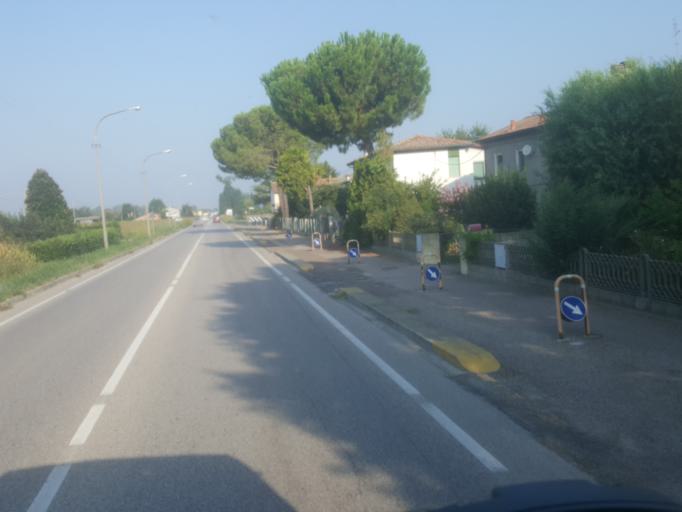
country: IT
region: Emilia-Romagna
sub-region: Provincia di Ravenna
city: Fornace Zarattini
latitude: 44.4494
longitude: 12.1209
